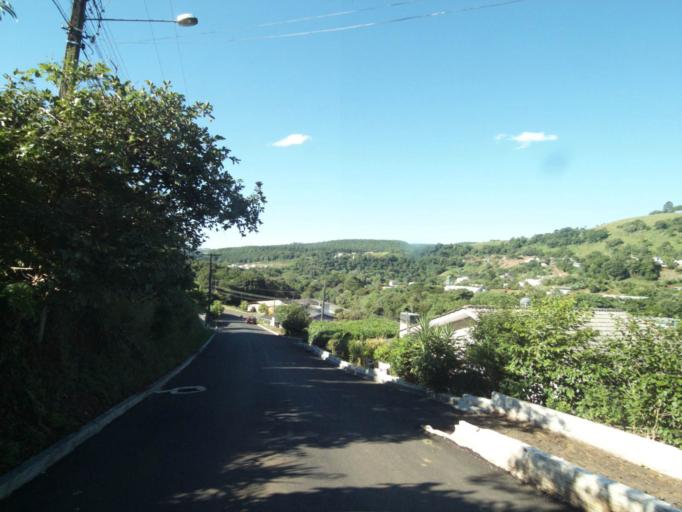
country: BR
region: Parana
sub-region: Ampere
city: Ampere
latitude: -26.1735
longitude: -53.3644
